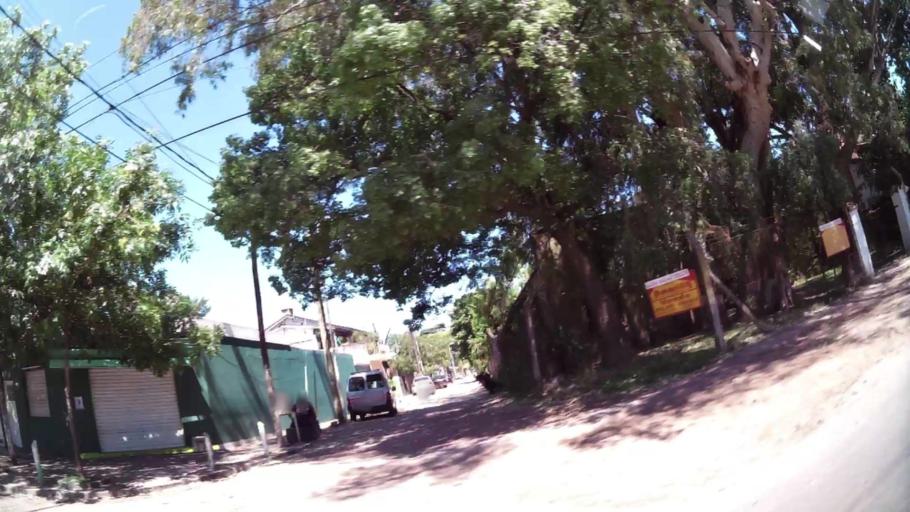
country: AR
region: Buenos Aires
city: Hurlingham
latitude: -34.4943
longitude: -58.6567
